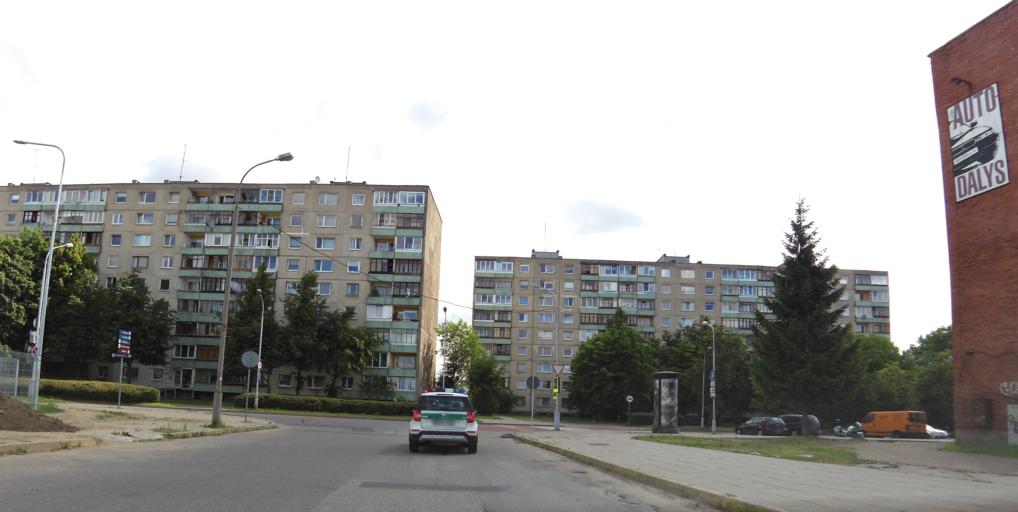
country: LT
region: Vilnius County
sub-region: Vilnius
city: Vilnius
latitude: 54.6994
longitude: 25.2859
